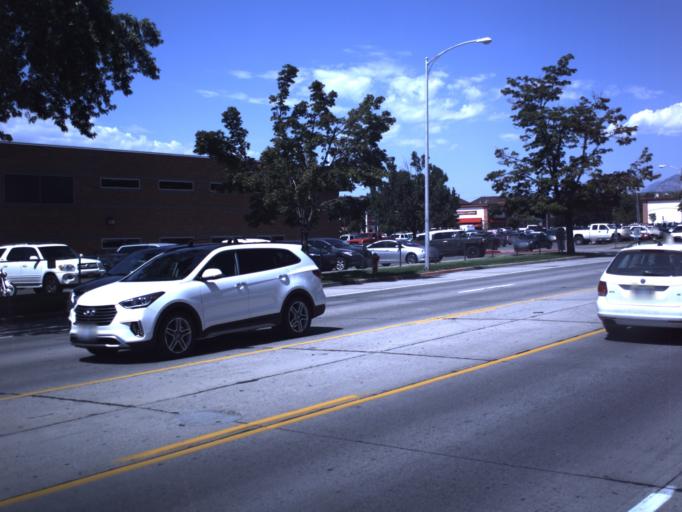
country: US
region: Utah
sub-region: Utah County
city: Provo
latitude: 40.2490
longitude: -111.6585
